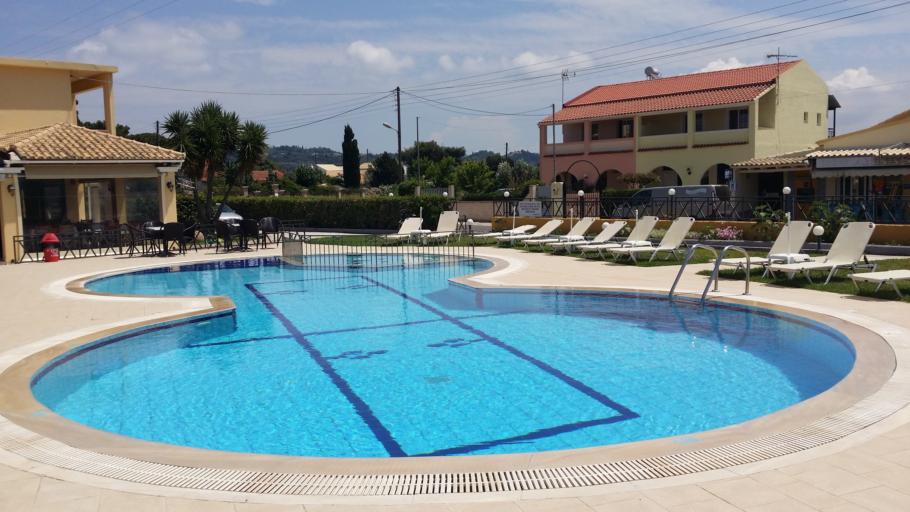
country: GR
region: Ionian Islands
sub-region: Nomos Kerkyras
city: Perivoli
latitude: 39.4280
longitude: 19.9486
